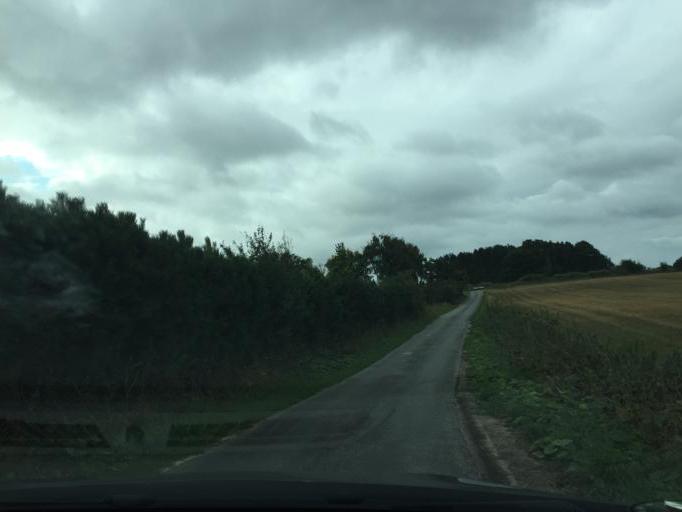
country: DK
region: South Denmark
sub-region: Assens Kommune
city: Harby
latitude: 55.1934
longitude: 10.1438
